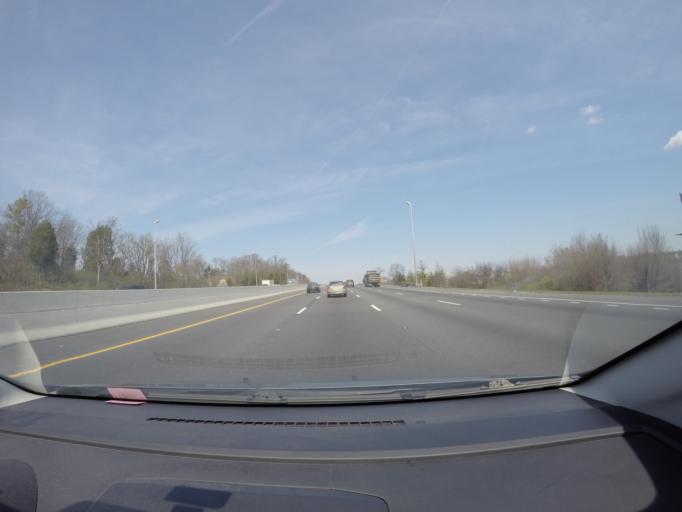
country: US
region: Tennessee
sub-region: Davidson County
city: Oak Hill
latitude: 36.0898
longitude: -86.7028
